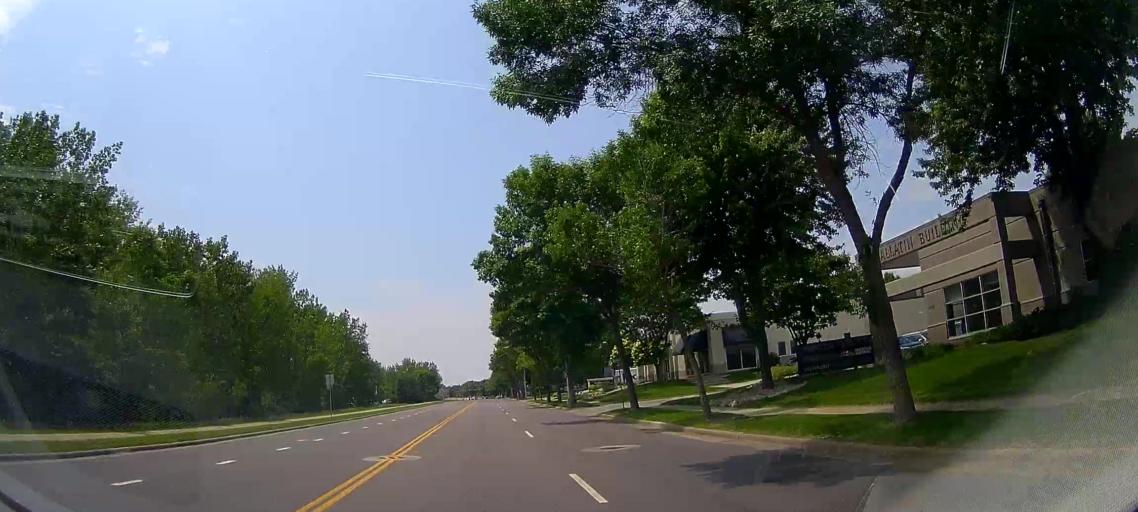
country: US
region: South Dakota
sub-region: Minnehaha County
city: Sioux Falls
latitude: 43.5084
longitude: -96.7530
